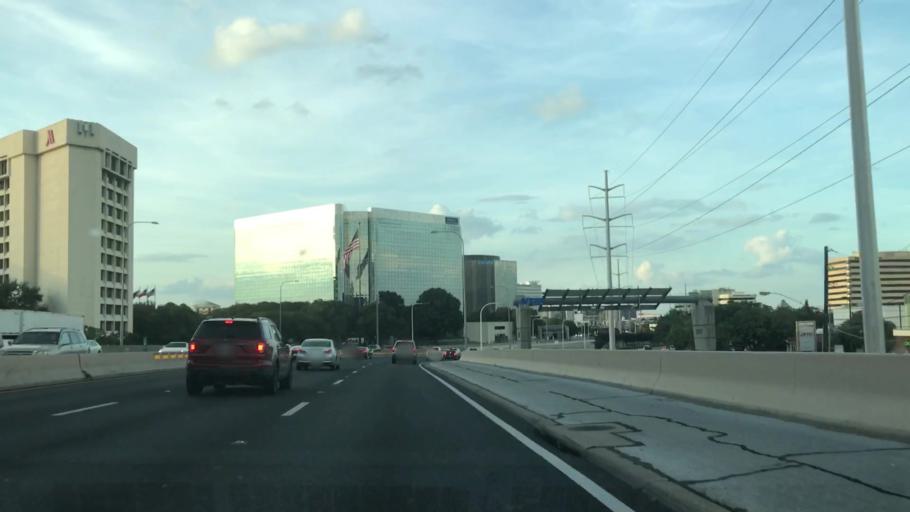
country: US
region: Texas
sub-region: Dallas County
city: Addison
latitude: 32.9497
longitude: -96.8233
